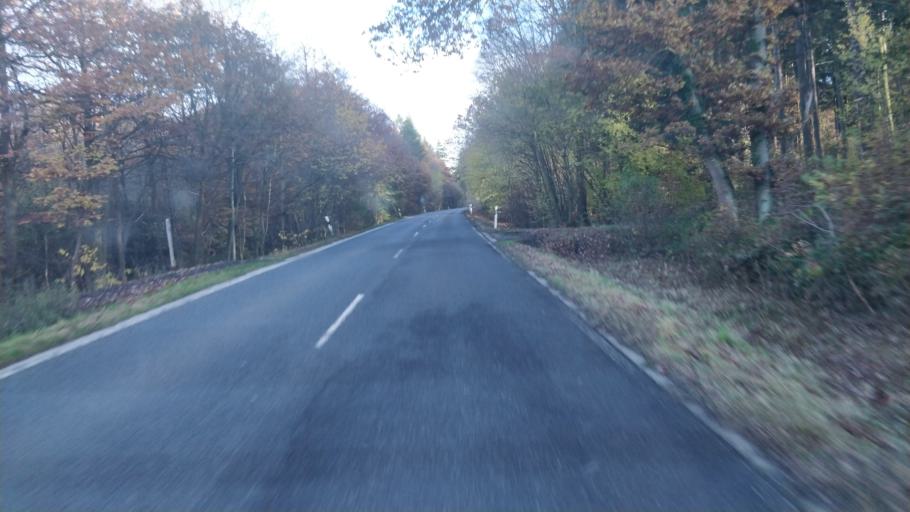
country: DE
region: North Rhine-Westphalia
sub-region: Regierungsbezirk Koln
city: Rheinbach
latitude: 50.6191
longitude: 6.8871
